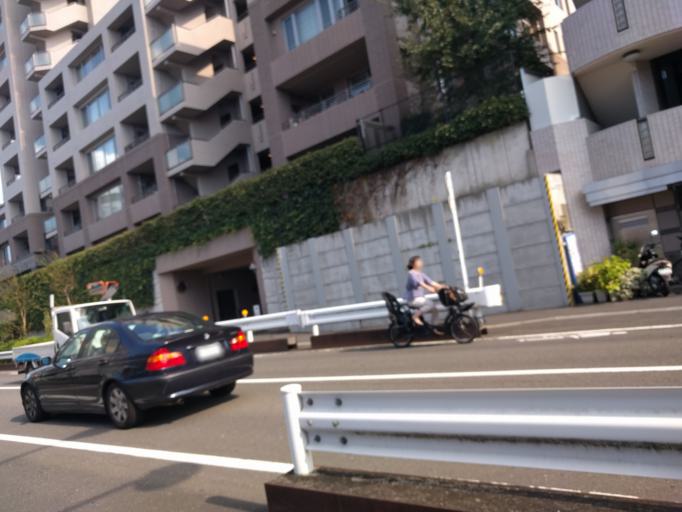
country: JP
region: Tokyo
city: Tokyo
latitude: 35.6284
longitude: 139.6370
